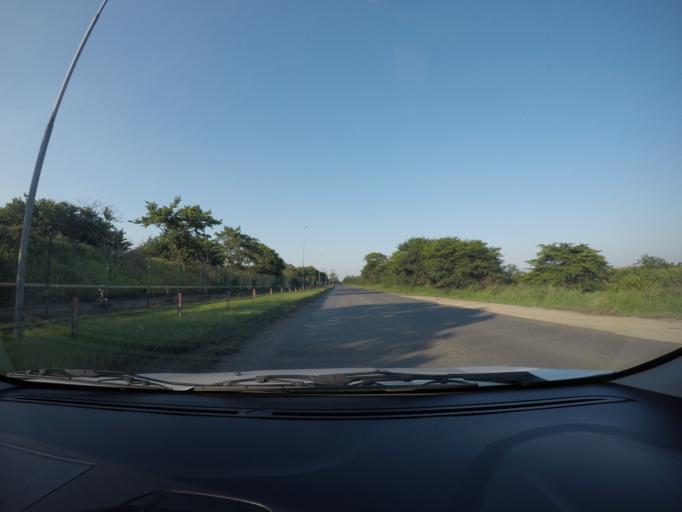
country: ZA
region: KwaZulu-Natal
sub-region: uThungulu District Municipality
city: Richards Bay
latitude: -28.7614
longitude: 32.0016
